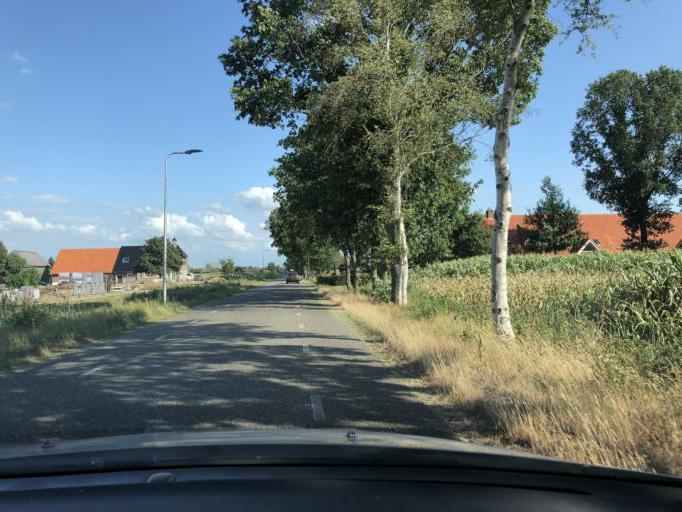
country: NL
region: Overijssel
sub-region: Gemeente Staphorst
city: Staphorst
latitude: 52.6210
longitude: 6.2470
